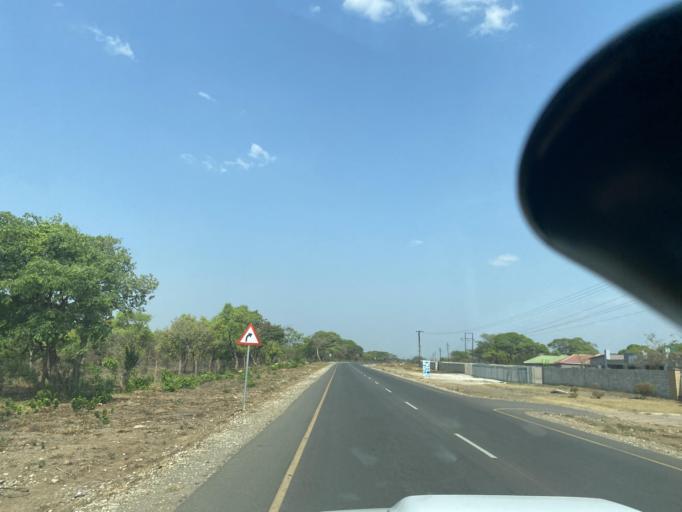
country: ZM
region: Lusaka
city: Lusaka
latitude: -15.3463
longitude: 28.0945
